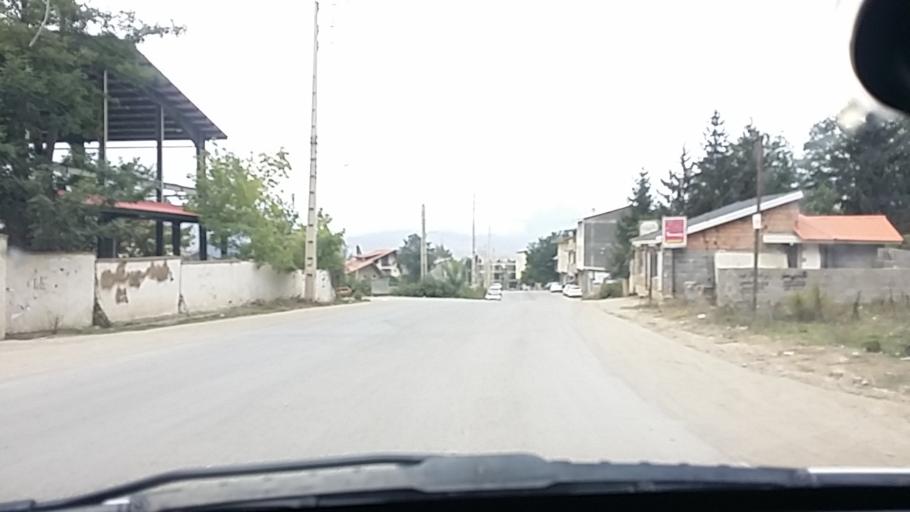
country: IR
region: Mazandaran
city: `Abbasabad
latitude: 36.4998
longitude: 51.1634
